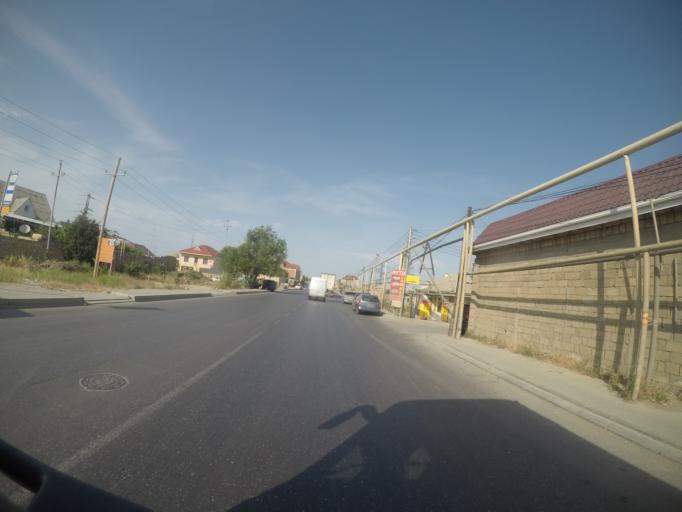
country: AZ
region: Baki
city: Bilajari
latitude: 40.4468
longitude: 49.7979
